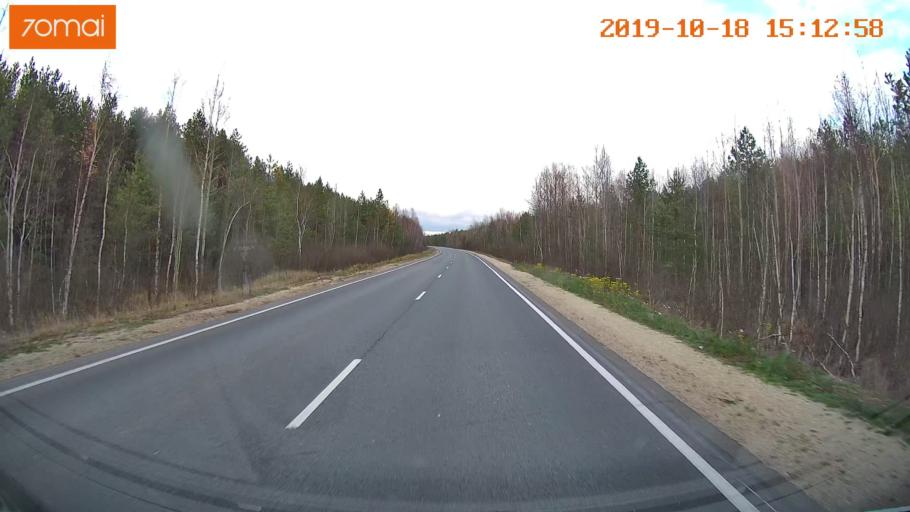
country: RU
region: Vladimir
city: Gus'-Khrustal'nyy
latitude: 55.5807
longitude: 40.7099
